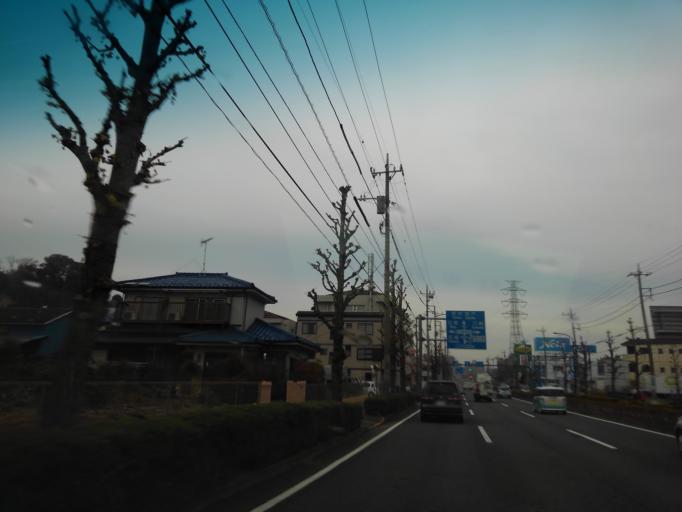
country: JP
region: Tokyo
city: Hino
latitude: 35.6418
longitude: 139.4512
